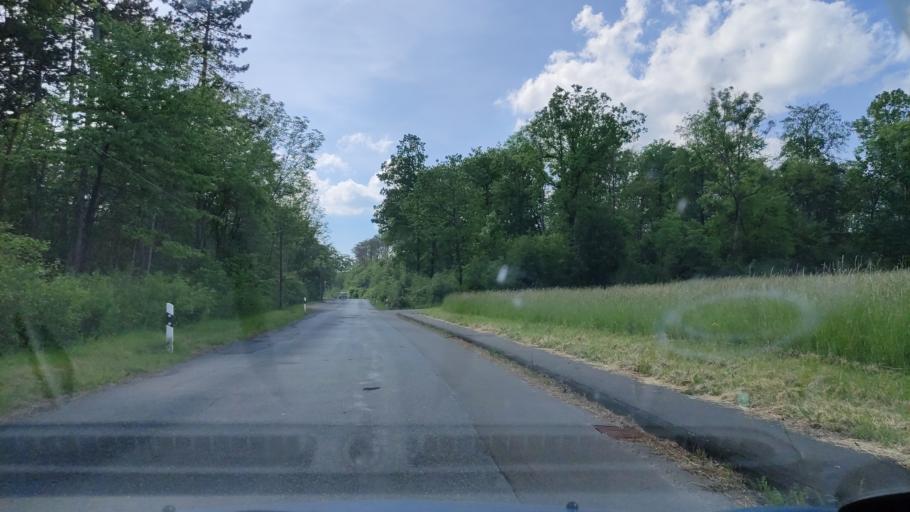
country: DE
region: Lower Saxony
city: Rosdorf
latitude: 51.5352
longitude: 9.8467
